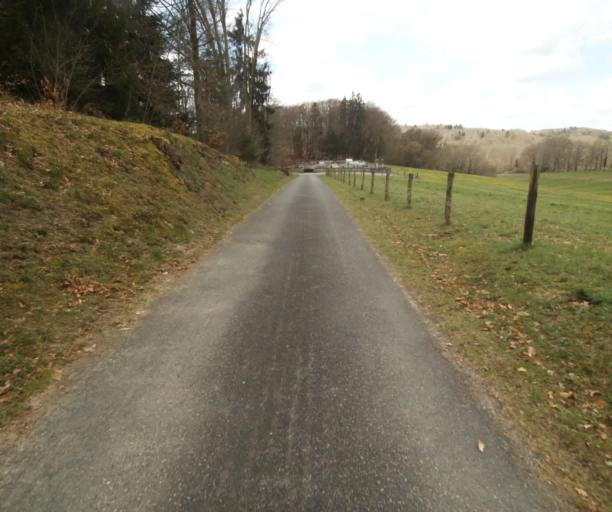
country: FR
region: Limousin
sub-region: Departement de la Correze
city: Laguenne
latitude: 45.2343
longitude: 1.8976
